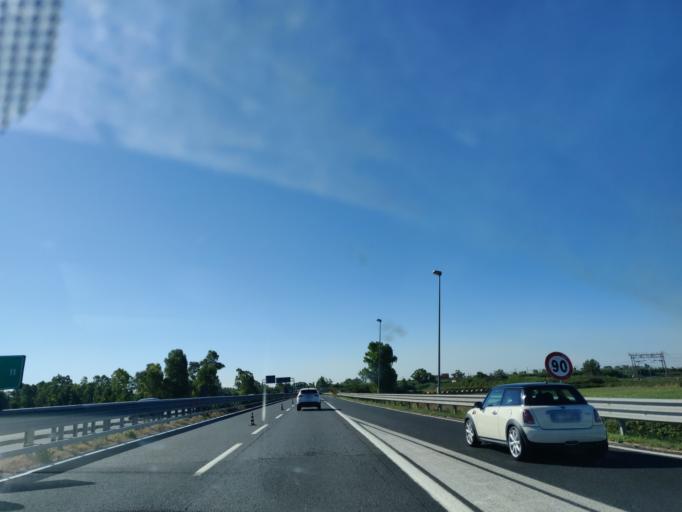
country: IT
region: Latium
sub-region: Citta metropolitana di Roma Capitale
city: Maccarese
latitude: 41.8869
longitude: 12.2311
